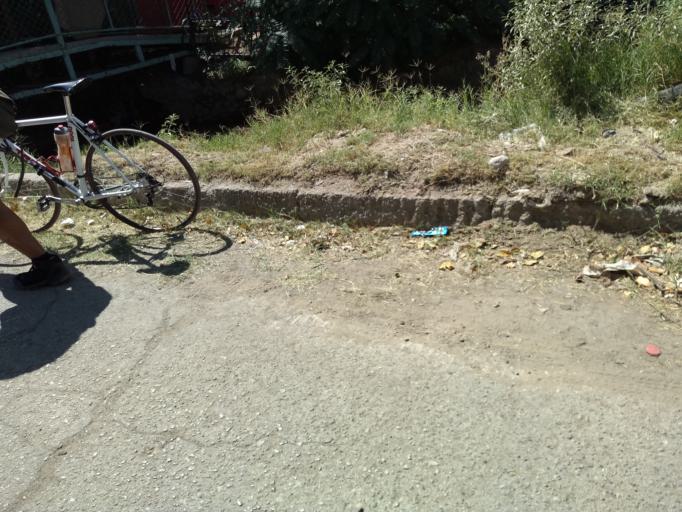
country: MX
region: Chihuahua
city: Ciudad Juarez
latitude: 31.7441
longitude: -106.4893
